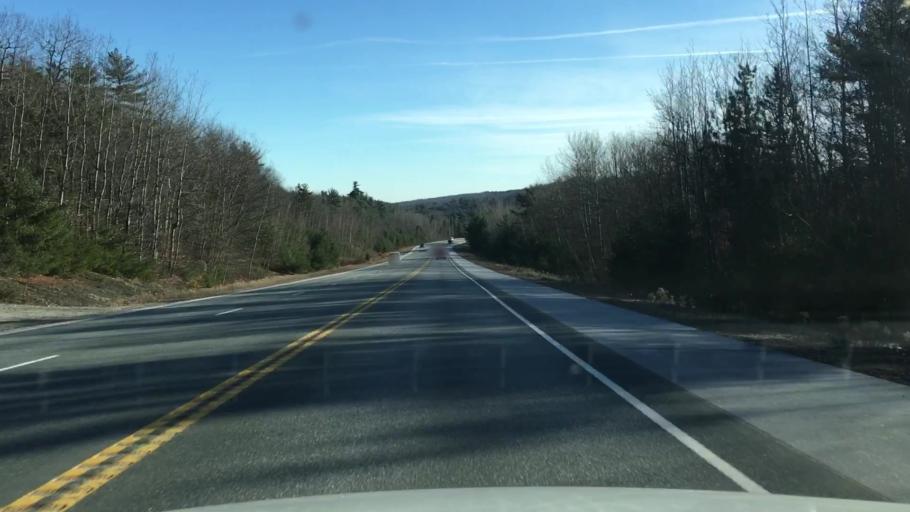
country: US
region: Maine
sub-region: Hancock County
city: Dedham
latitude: 44.6858
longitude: -68.5819
